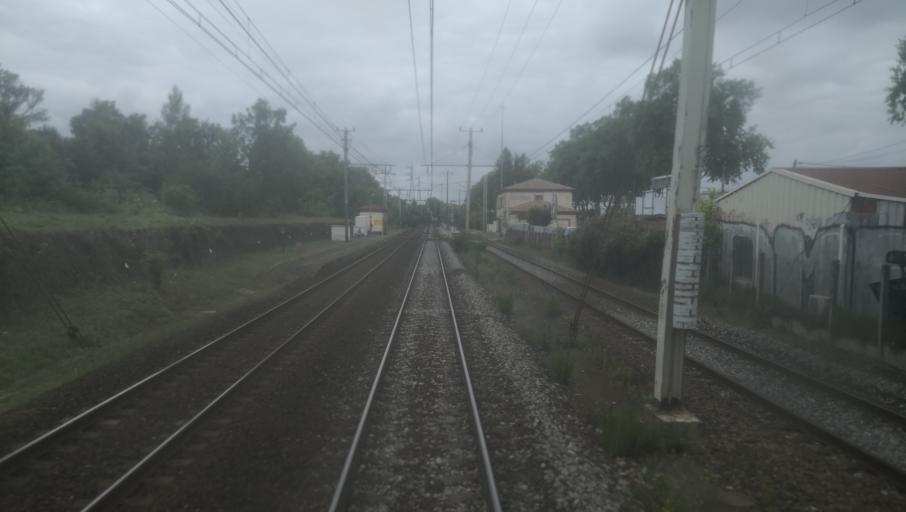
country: FR
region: Midi-Pyrenees
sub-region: Departement de la Haute-Garonne
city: Aucamville
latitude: 43.6630
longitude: 1.4147
